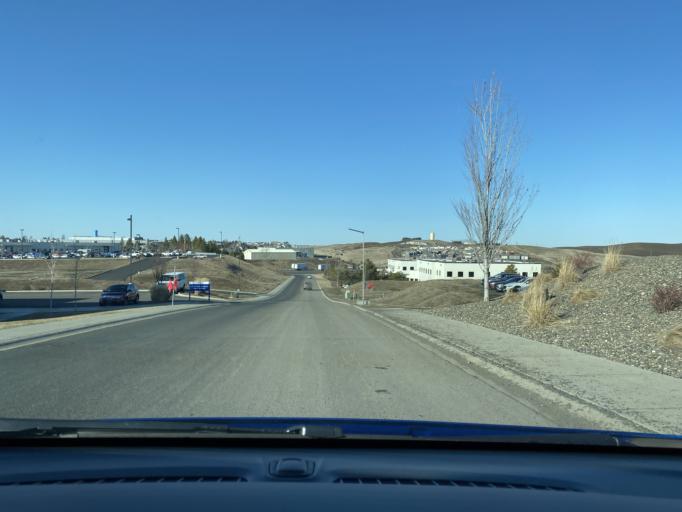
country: US
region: Washington
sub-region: Whitman County
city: Pullman
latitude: 46.7523
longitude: -117.1577
